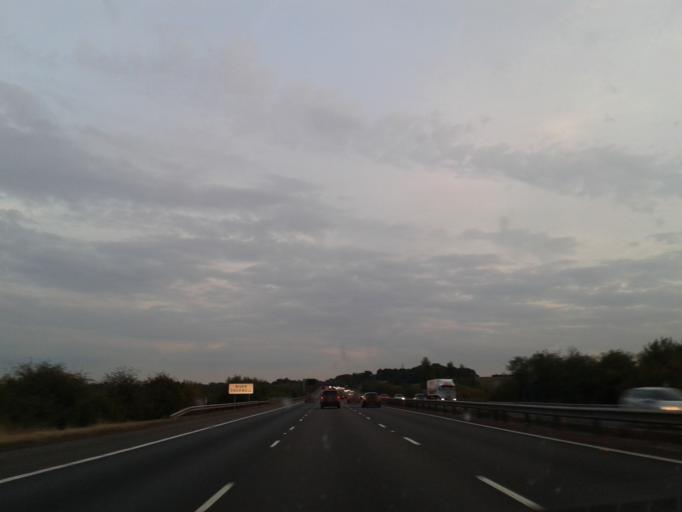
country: GB
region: England
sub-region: Oxfordshire
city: Adderbury
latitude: 52.0478
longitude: -1.3054
